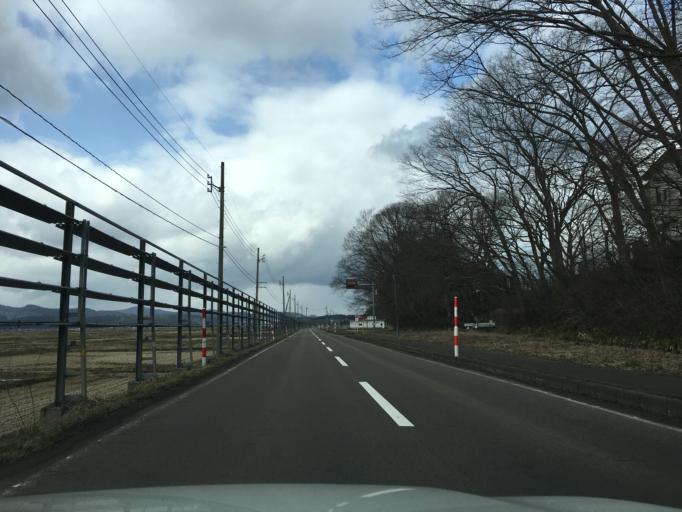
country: JP
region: Akita
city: Takanosu
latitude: 40.1462
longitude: 140.3440
